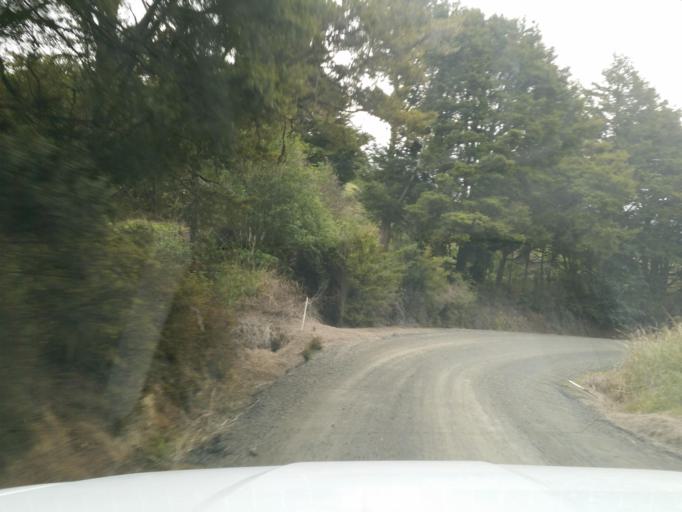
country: NZ
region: Northland
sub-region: Kaipara District
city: Dargaville
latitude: -35.7582
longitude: 173.9269
